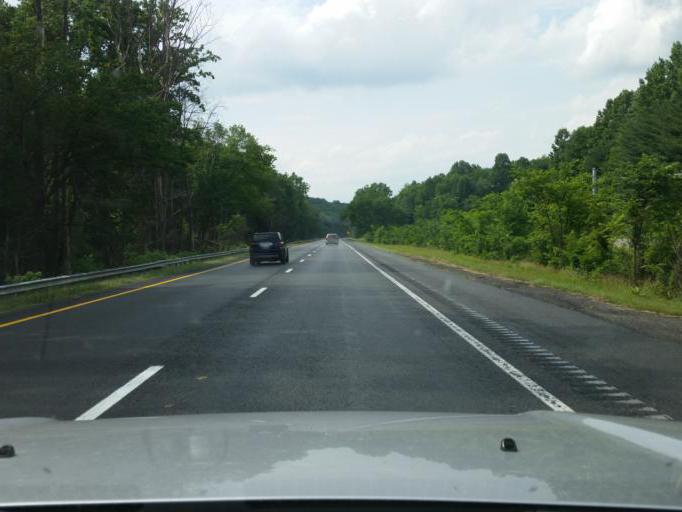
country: US
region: Maryland
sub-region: Montgomery County
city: Clarksburg
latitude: 39.2615
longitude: -77.3088
